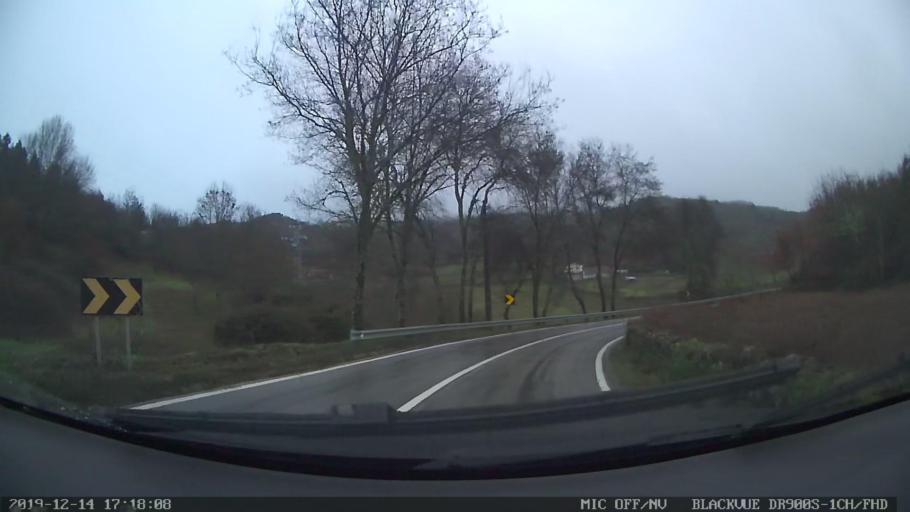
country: PT
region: Vila Real
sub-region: Vila Pouca de Aguiar
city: Vila Pouca de Aguiar
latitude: 41.4962
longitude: -7.6365
